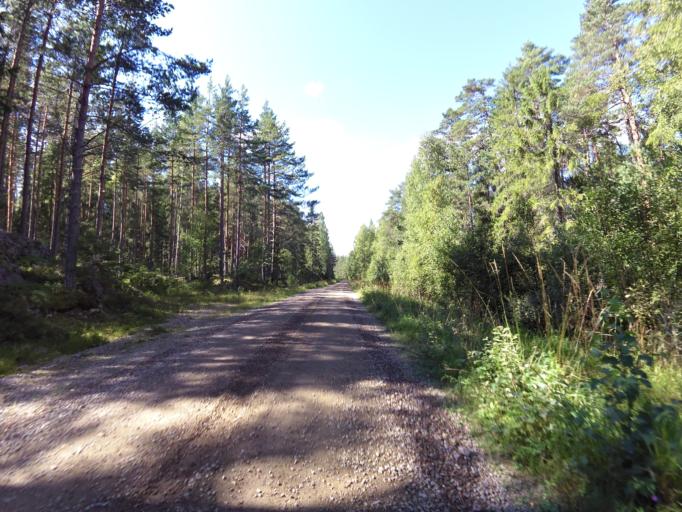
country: SE
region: Gaevleborg
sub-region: Ockelbo Kommun
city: Ockelbo
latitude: 60.7972
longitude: 16.8377
